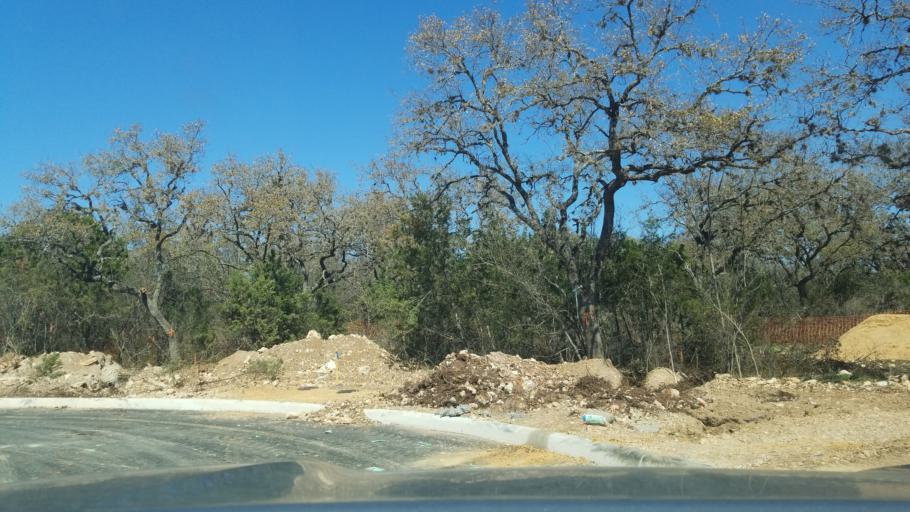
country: US
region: Texas
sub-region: Bexar County
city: Helotes
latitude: 29.5615
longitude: -98.6755
